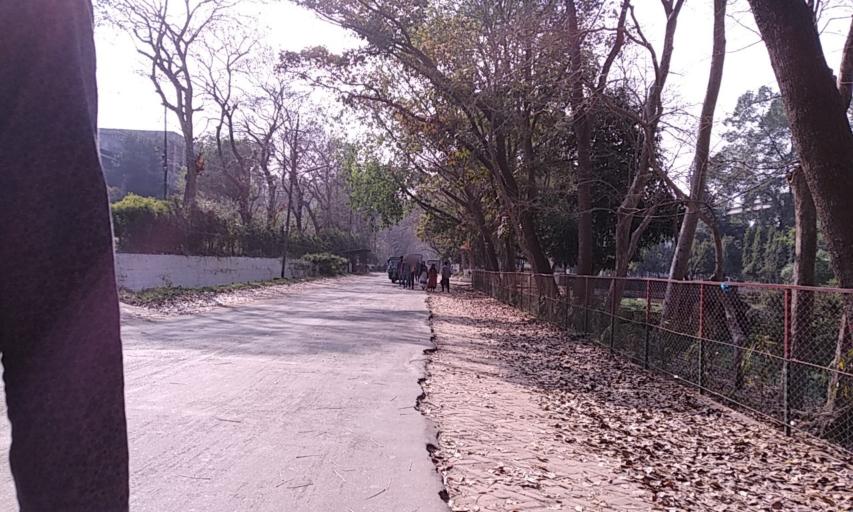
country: BD
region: Chittagong
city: Chittagong
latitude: 22.4711
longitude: 91.7858
